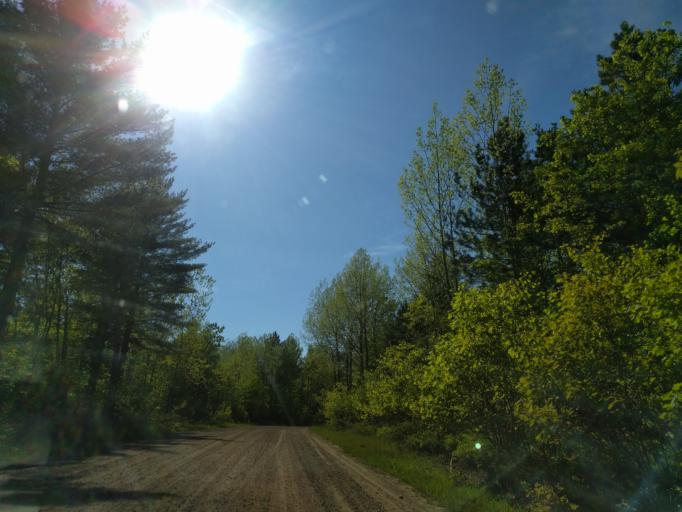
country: US
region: Michigan
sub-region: Marquette County
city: Gwinn
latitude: 46.2696
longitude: -87.3658
